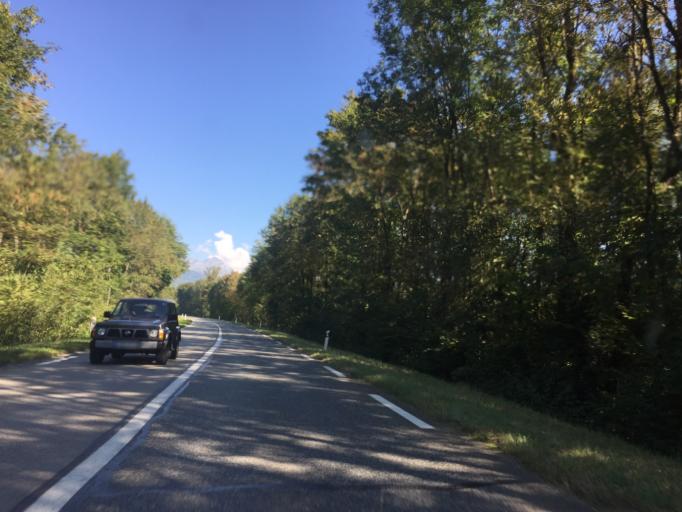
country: FR
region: Rhone-Alpes
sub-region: Departement de la Savoie
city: Frontenex
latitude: 45.6322
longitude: 6.3288
